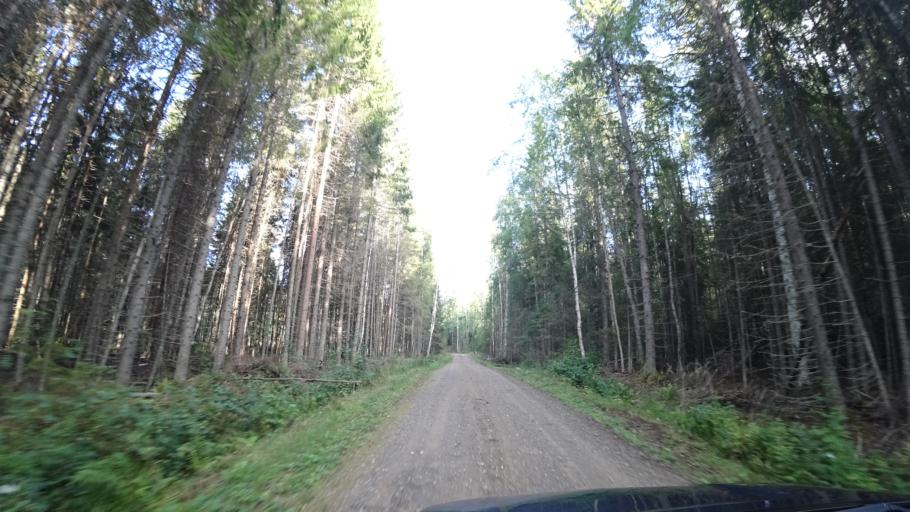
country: FI
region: Paijanne Tavastia
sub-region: Lahti
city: Auttoinen
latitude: 61.2193
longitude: 25.2074
